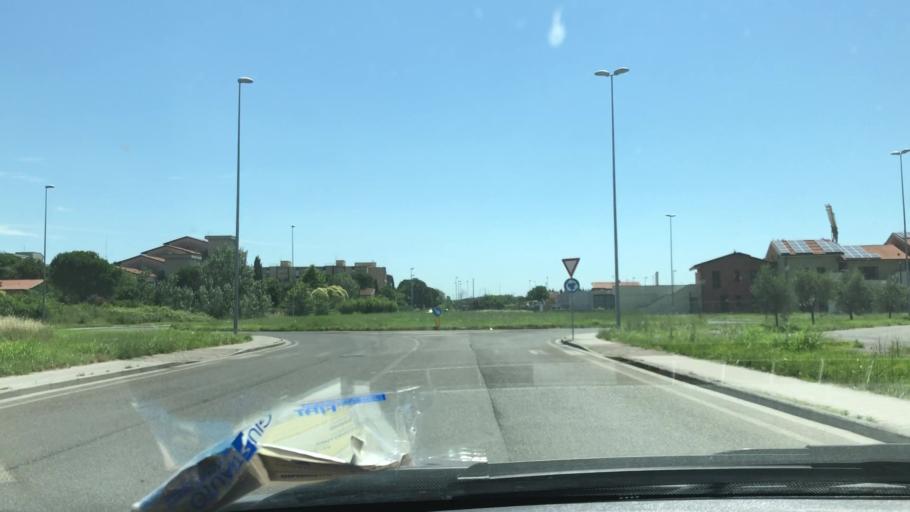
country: IT
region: Tuscany
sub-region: Province of Pisa
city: Pontedera
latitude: 43.6558
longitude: 10.6226
